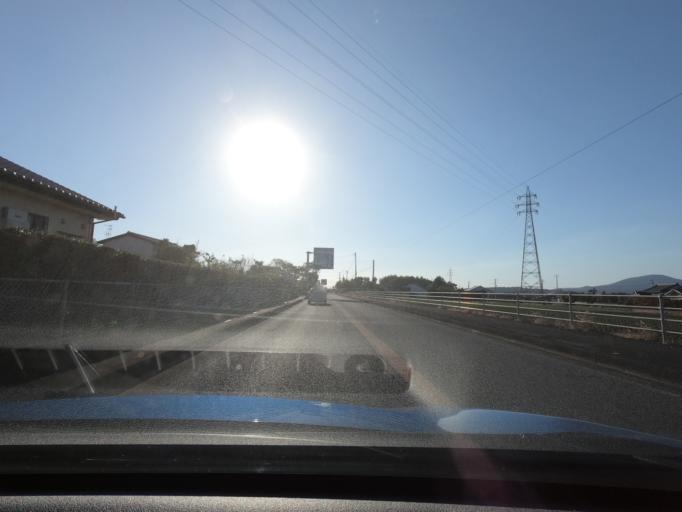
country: JP
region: Kagoshima
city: Izumi
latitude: 32.0950
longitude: 130.2981
